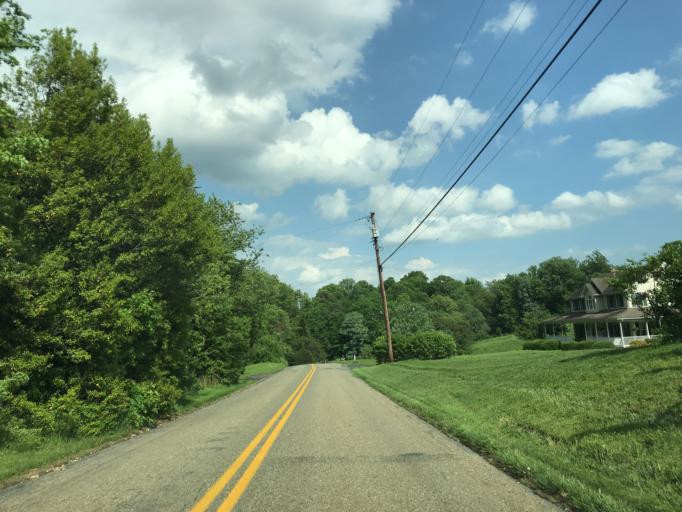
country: US
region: Maryland
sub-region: Harford County
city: Bel Air North
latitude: 39.6130
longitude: -76.3733
